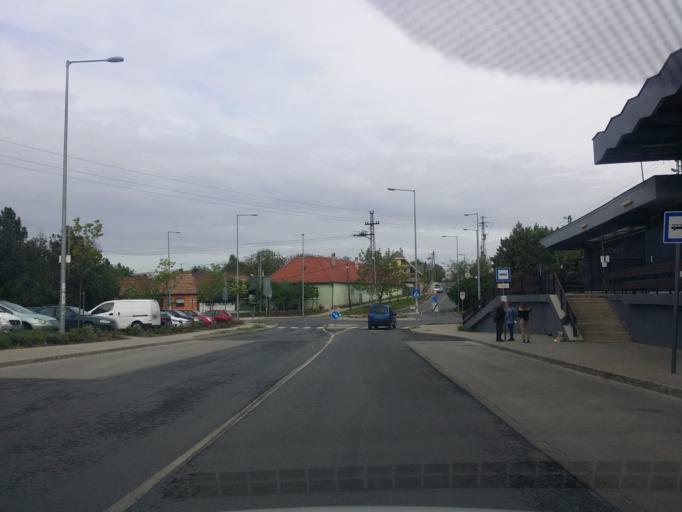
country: HU
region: Pest
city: Biatorbagy
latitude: 47.4797
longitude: 18.8342
